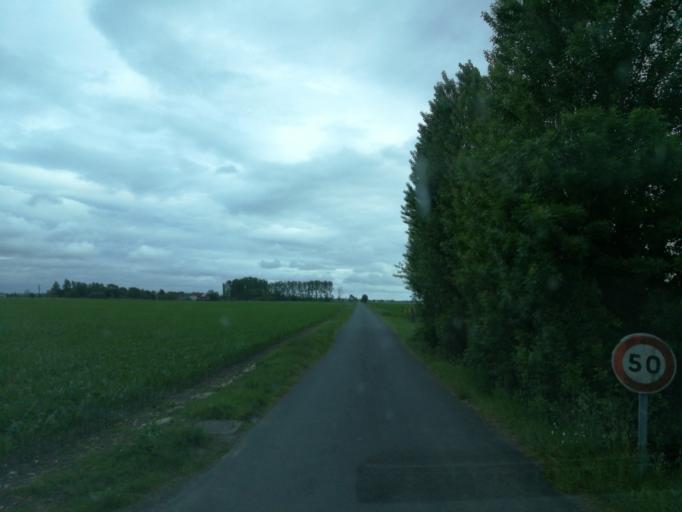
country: FR
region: Pays de la Loire
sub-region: Departement de la Vendee
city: Le Langon
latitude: 46.3718
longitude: -0.9308
